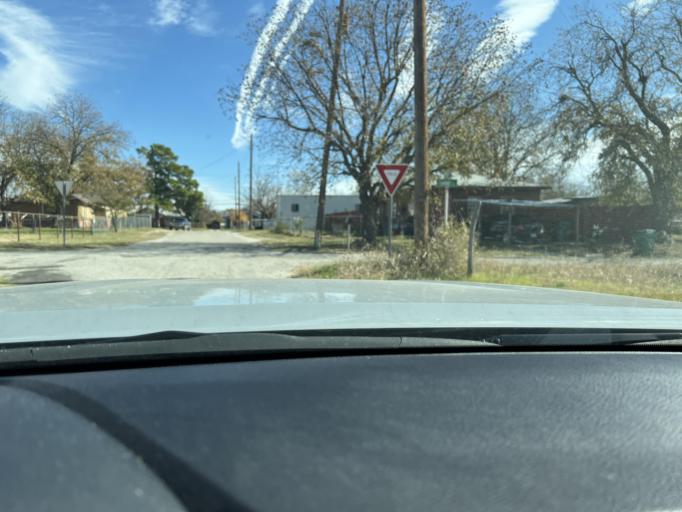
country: US
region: Texas
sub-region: Eastland County
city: Eastland
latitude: 32.3878
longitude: -98.8192
